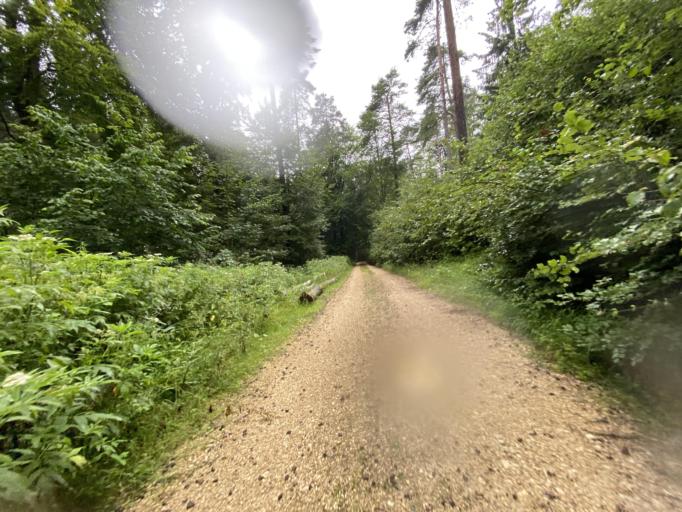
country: DE
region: Baden-Wuerttemberg
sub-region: Tuebingen Region
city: Sigmaringen
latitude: 48.1240
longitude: 9.2234
